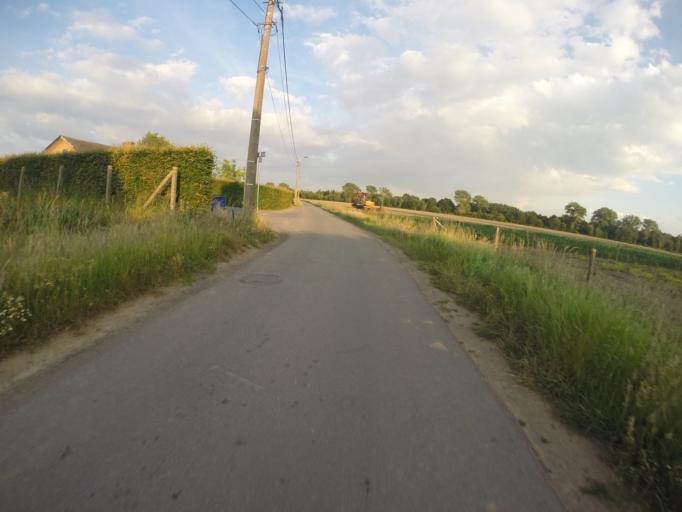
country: BE
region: Flanders
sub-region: Provincie West-Vlaanderen
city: Beernem
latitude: 51.1443
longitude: 3.3170
